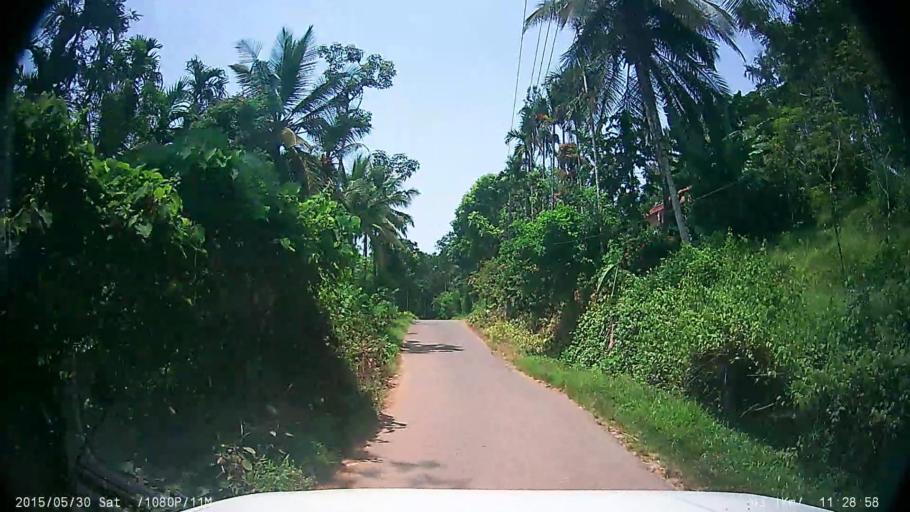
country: IN
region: Kerala
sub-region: Wayanad
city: Panamaram
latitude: 11.8109
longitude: 76.0473
